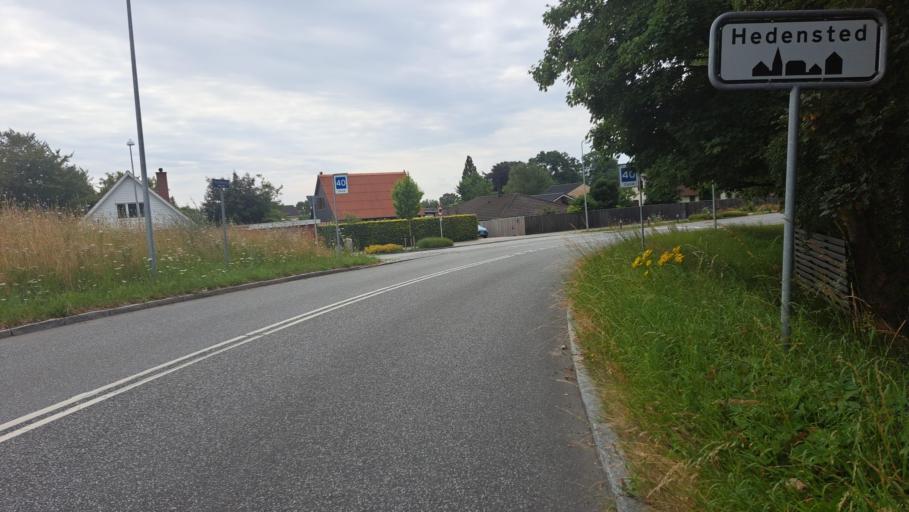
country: DK
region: Central Jutland
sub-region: Hedensted Kommune
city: Hedensted
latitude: 55.7750
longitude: 9.7082
